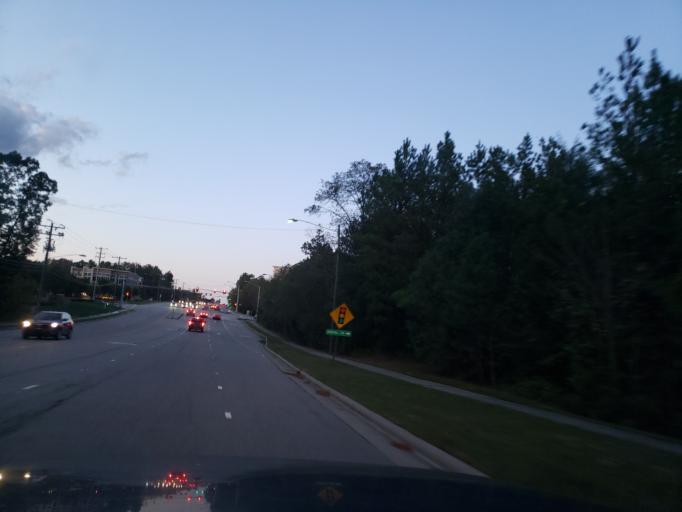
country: US
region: North Carolina
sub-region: Orange County
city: Chapel Hill
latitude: 35.8996
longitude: -78.9593
